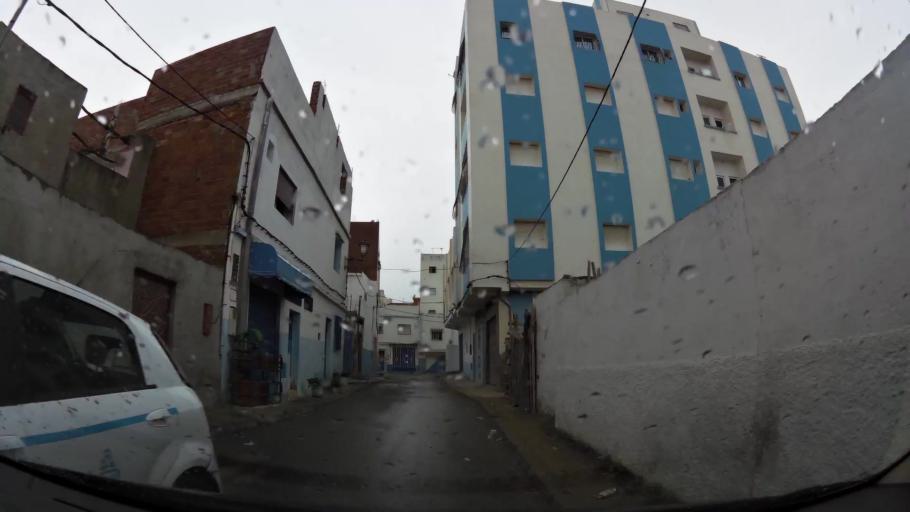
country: MA
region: Tanger-Tetouan
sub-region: Tetouan
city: Martil
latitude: 35.6222
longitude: -5.2778
